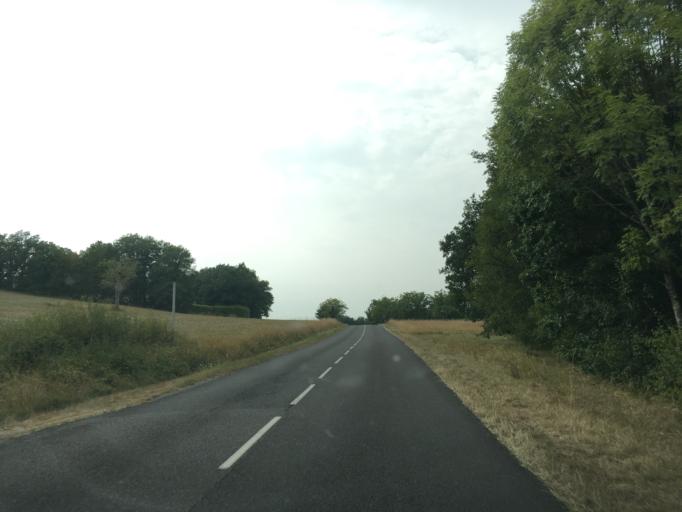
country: FR
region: Midi-Pyrenees
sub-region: Departement du Lot
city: Souillac
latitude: 44.8450
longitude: 1.5462
